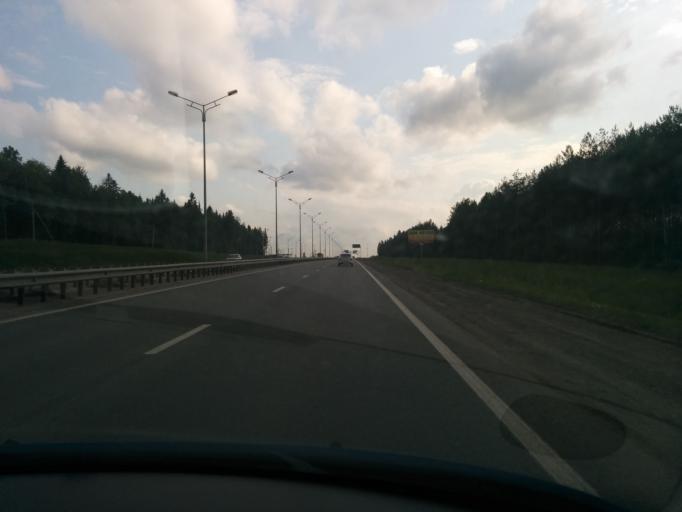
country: RU
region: Perm
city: Ferma
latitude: 58.0065
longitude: 56.3952
